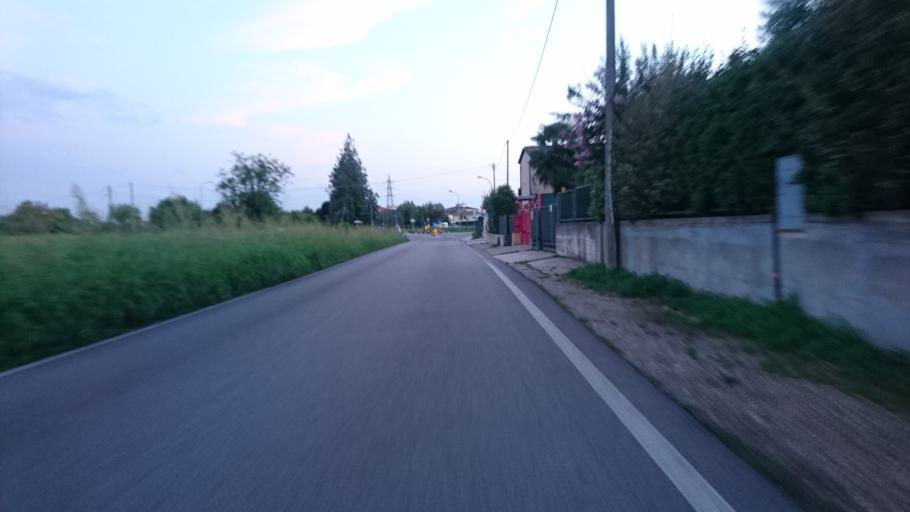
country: IT
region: Veneto
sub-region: Provincia di Padova
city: Selvazzano Dentro
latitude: 45.3726
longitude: 11.7993
